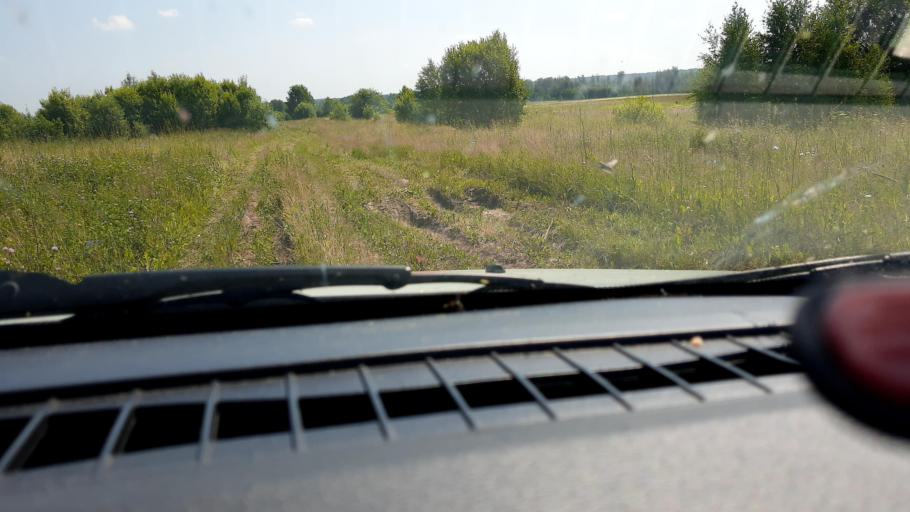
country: RU
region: Nizjnij Novgorod
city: Sharanga
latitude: 57.0456
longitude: 46.7348
